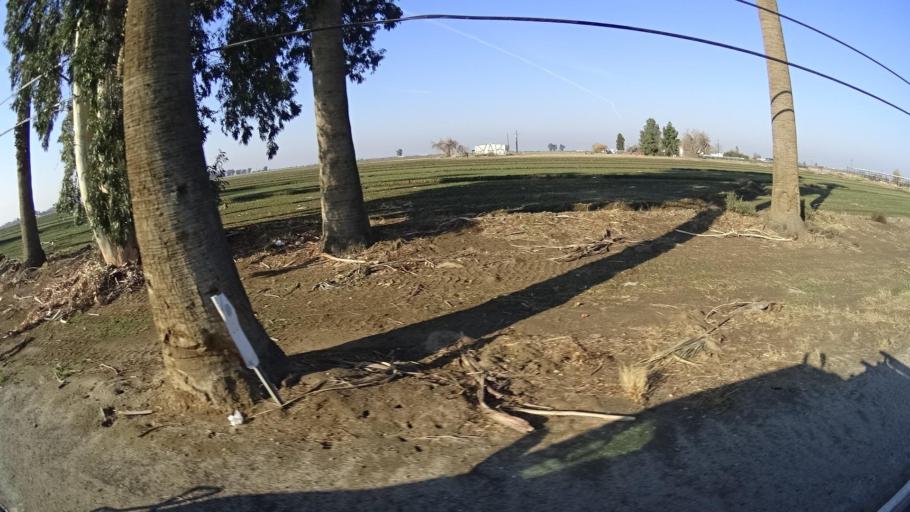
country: US
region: California
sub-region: Kern County
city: Greenfield
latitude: 35.2440
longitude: -119.0030
